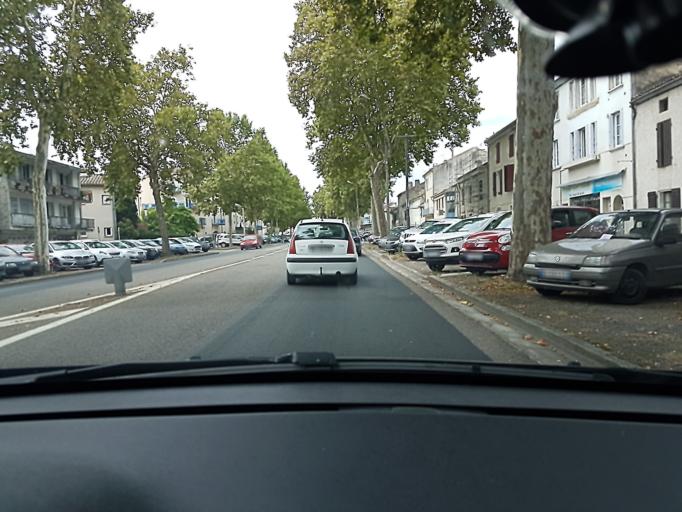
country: FR
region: Aquitaine
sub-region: Departement du Lot-et-Garonne
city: Nerac
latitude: 44.1375
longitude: 0.3364
